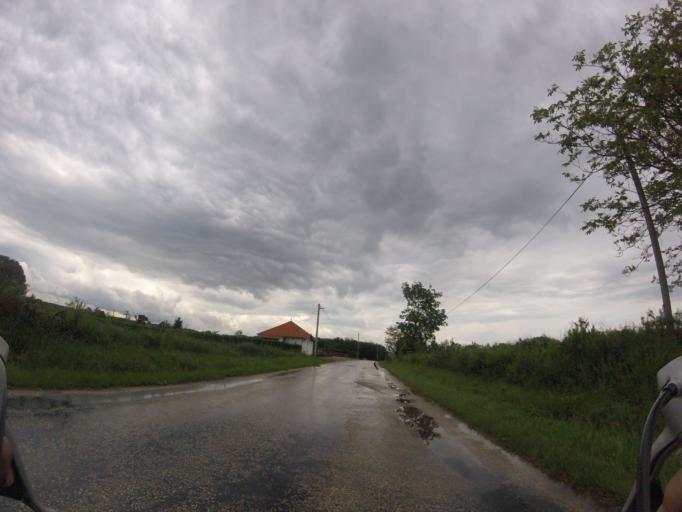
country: HU
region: Baranya
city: Pellerd
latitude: 45.9653
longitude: 18.1820
